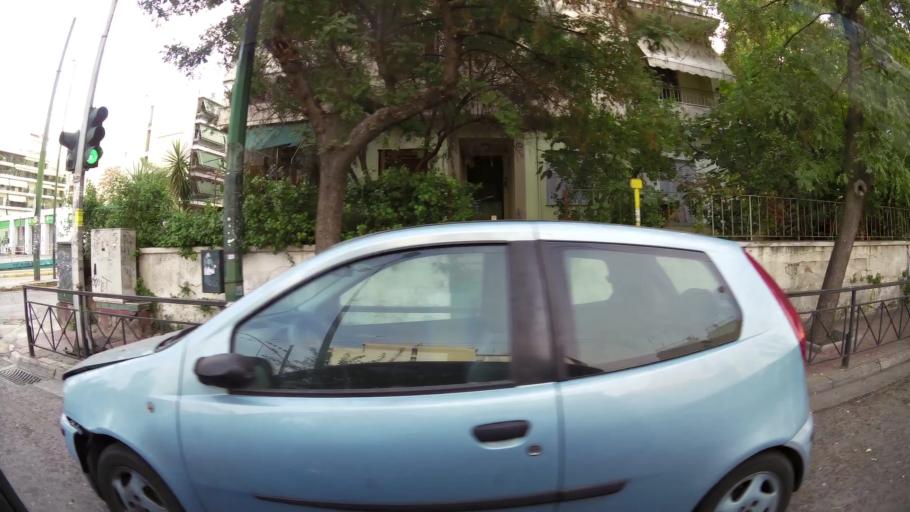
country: GR
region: Attica
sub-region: Nomarchia Athinas
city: Nea Chalkidona
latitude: 38.0208
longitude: 23.7296
